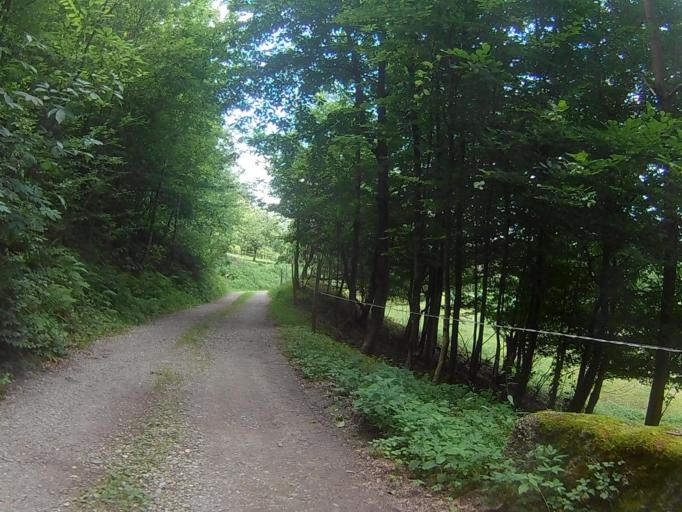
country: SI
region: Ruse
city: Ruse
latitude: 46.5334
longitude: 15.5046
